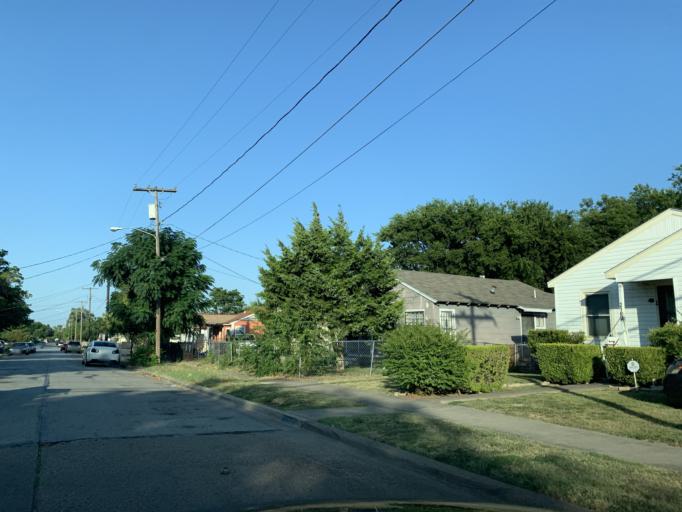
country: US
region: Texas
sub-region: Dallas County
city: Dallas
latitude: 32.7068
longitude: -96.7968
